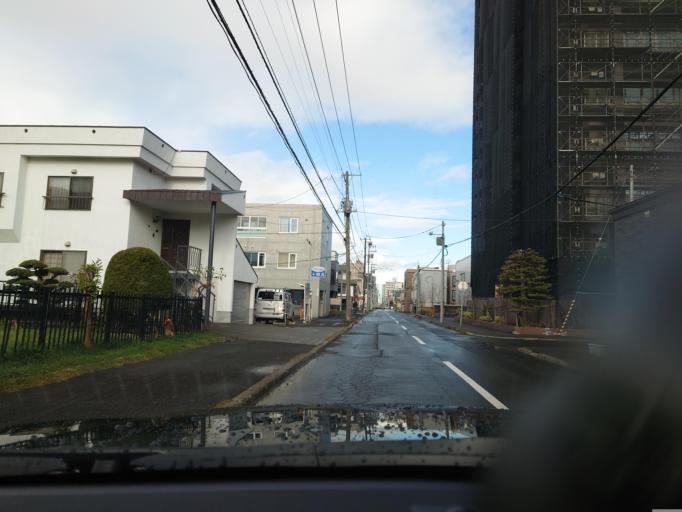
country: JP
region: Hokkaido
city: Sapporo
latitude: 43.0327
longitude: 141.3461
